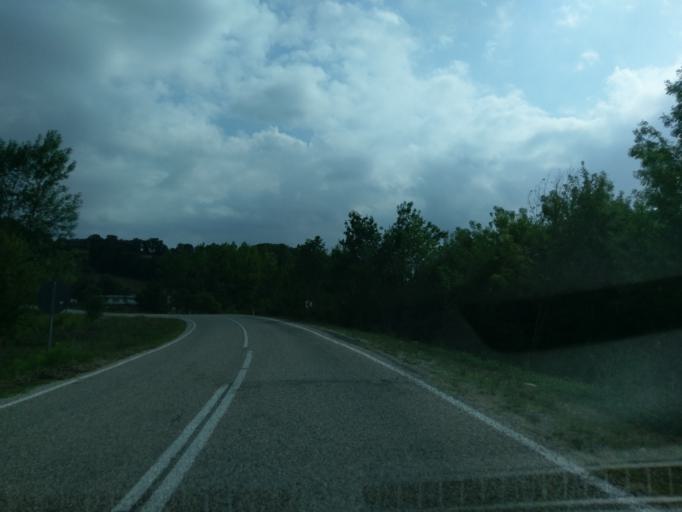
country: TR
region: Sinop
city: Erfelek
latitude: 41.9597
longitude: 34.8346
